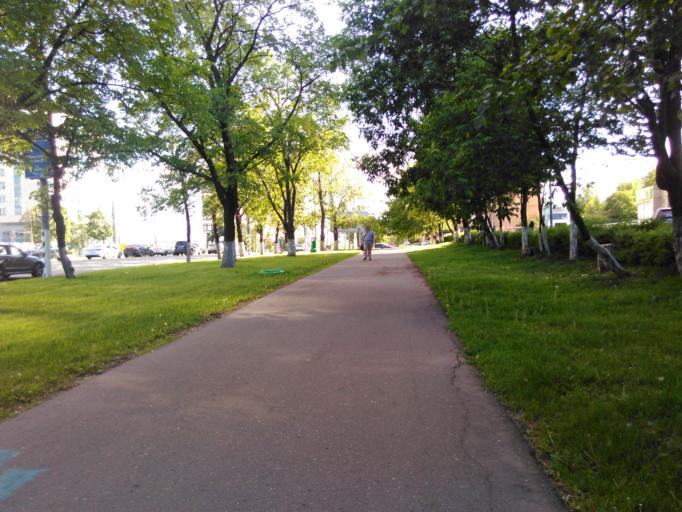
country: RU
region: Moskovskaya
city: Cheremushki
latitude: 55.6654
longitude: 37.5490
